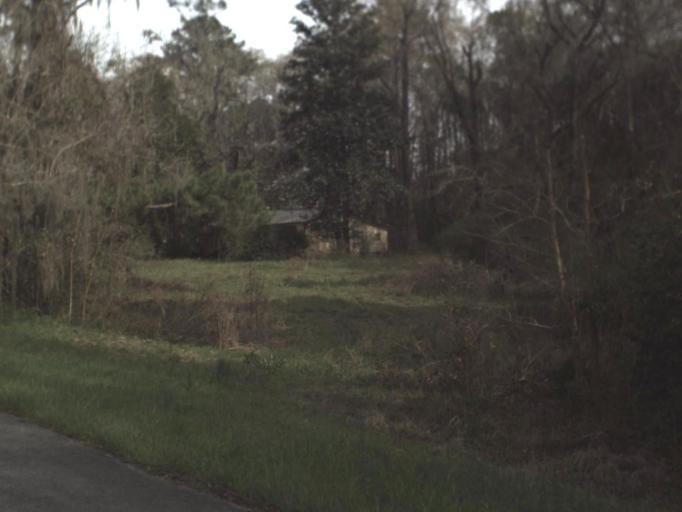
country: US
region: Florida
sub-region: Jefferson County
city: Monticello
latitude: 30.5406
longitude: -83.9140
